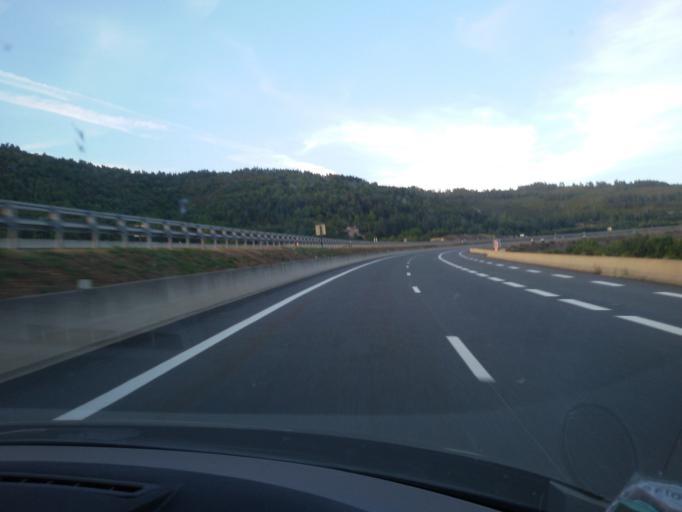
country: FR
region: Midi-Pyrenees
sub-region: Departement de l'Aveyron
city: Severac-le-Chateau
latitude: 44.3438
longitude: 3.0856
